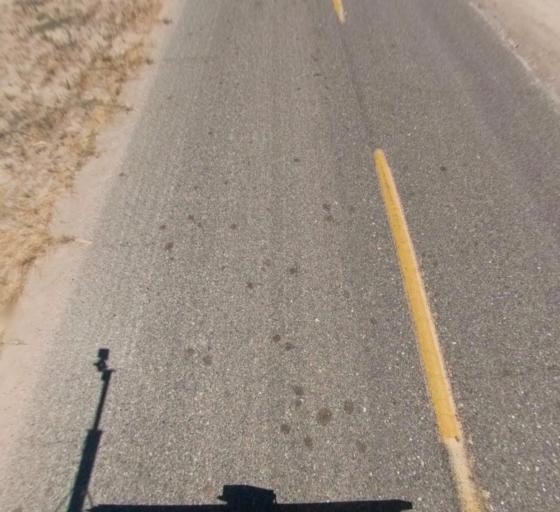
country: US
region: California
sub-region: Fresno County
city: Biola
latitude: 36.8475
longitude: -120.0192
